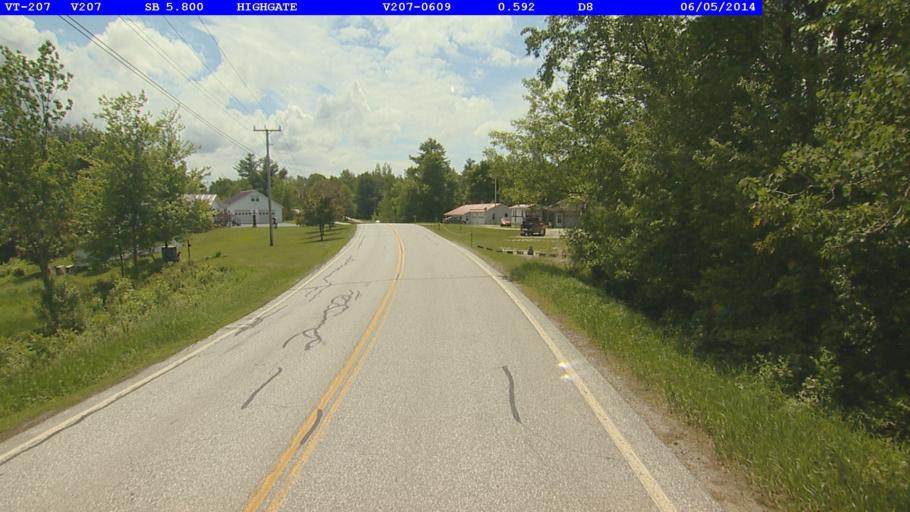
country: US
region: Vermont
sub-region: Franklin County
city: Swanton
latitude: 44.9198
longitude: -73.0548
